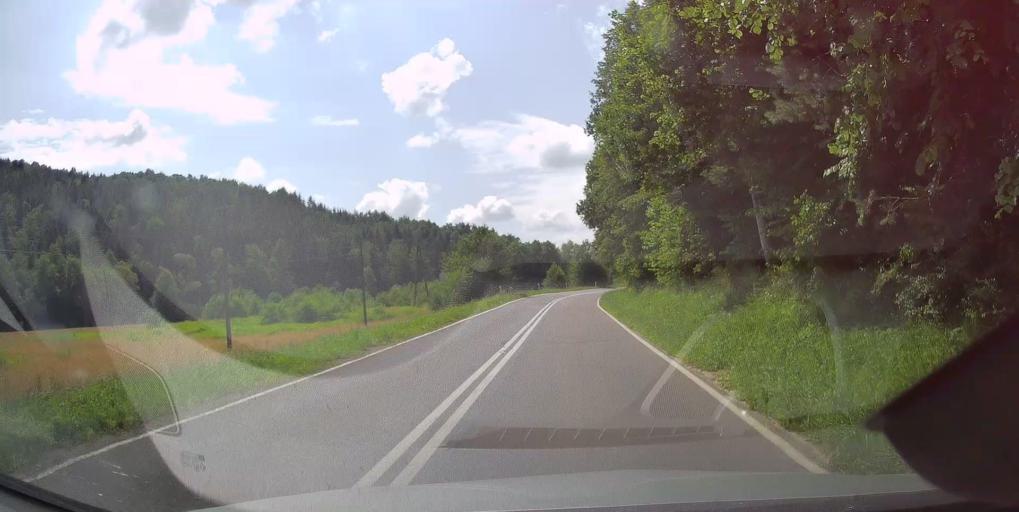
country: PL
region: Lesser Poland Voivodeship
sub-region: Powiat tarnowski
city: Zakliczyn
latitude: 49.8119
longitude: 20.7989
